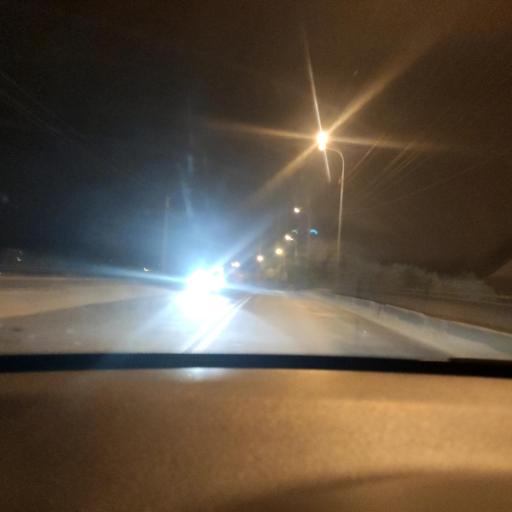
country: RU
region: Samara
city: Smyshlyayevka
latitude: 53.2208
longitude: 50.2899
